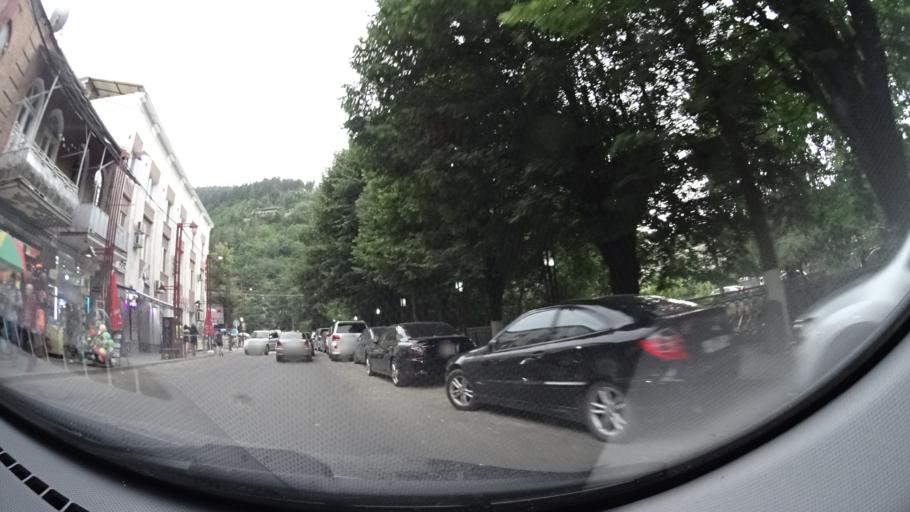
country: GE
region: Samtskhe-Javakheti
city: Borjomi
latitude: 41.8396
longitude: 43.3868
